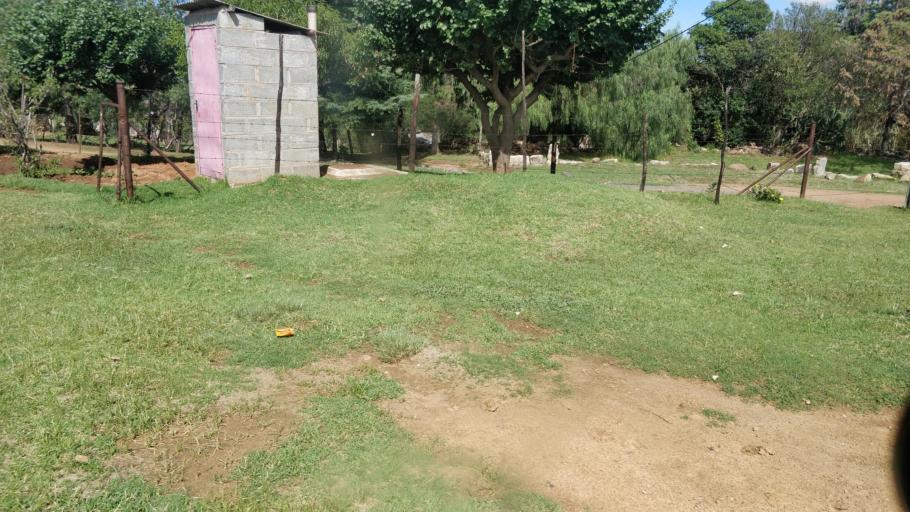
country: LS
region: Maseru
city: Nako
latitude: -29.6246
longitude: 27.5128
